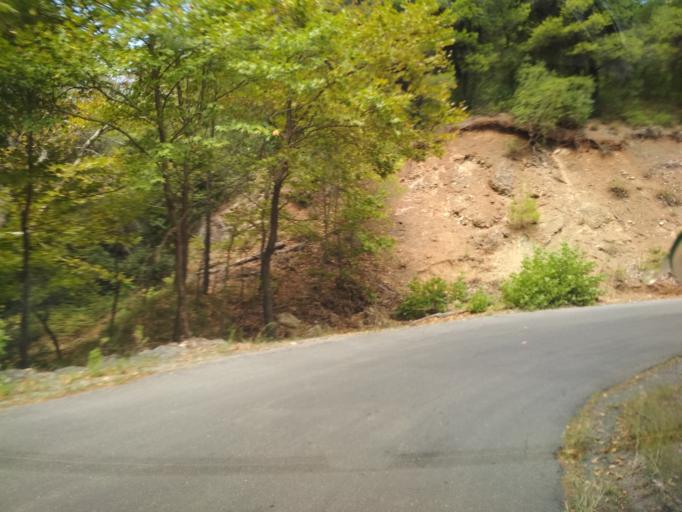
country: GR
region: Central Greece
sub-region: Nomos Evvoias
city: Roviai
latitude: 38.8391
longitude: 23.2841
